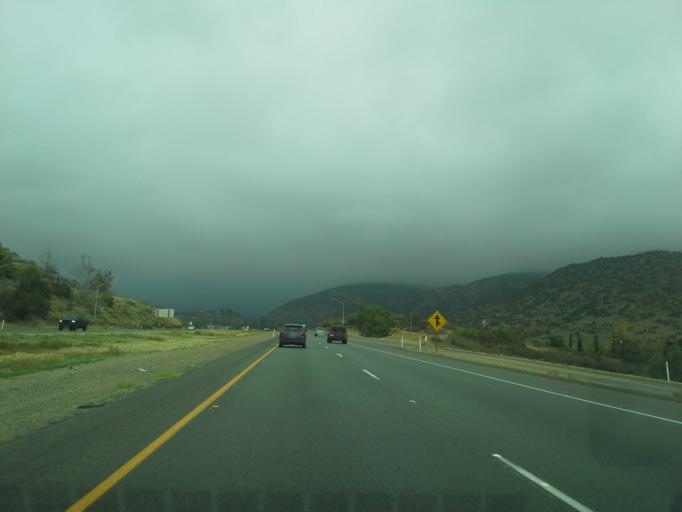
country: US
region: California
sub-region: San Diego County
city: Crest
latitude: 32.8448
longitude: -116.8801
